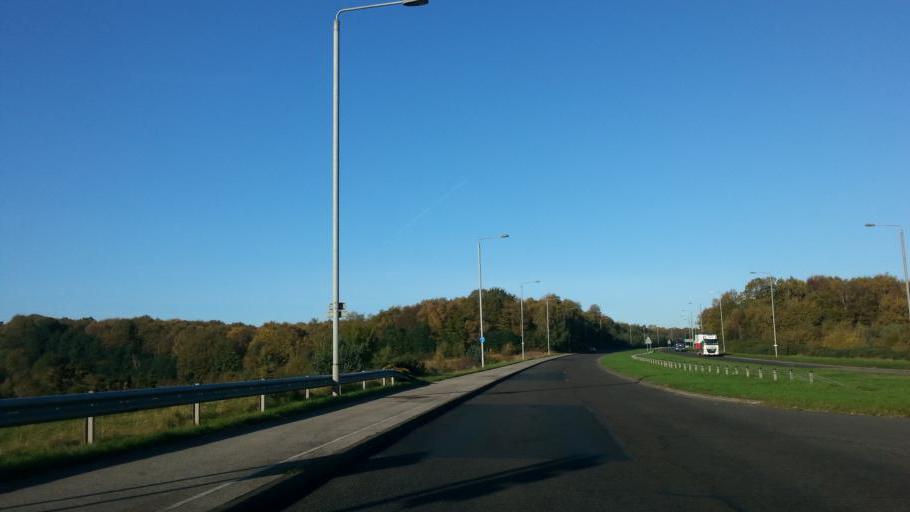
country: GB
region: England
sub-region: Nottinghamshire
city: Rainworth
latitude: 53.1223
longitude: -1.1171
